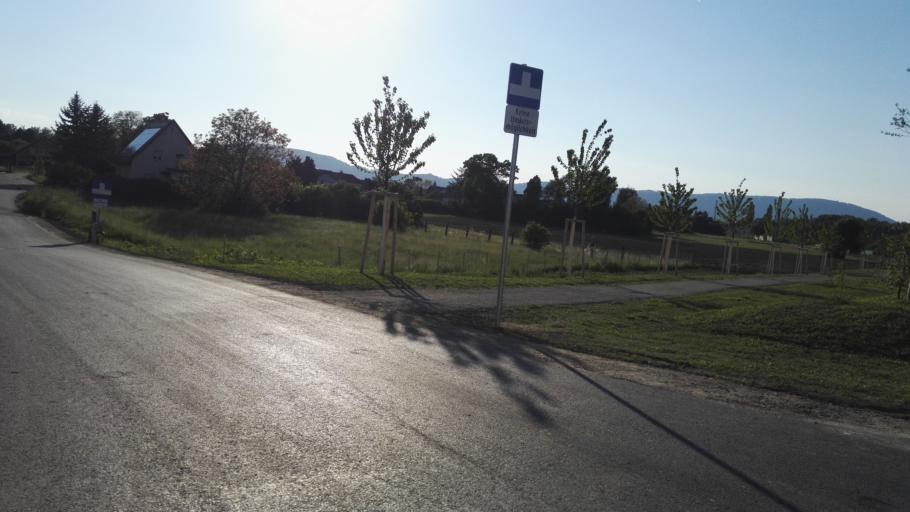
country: AT
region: Styria
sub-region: Politischer Bezirk Graz-Umgebung
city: Feldkirchen bei Graz
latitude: 47.0311
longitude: 15.4611
